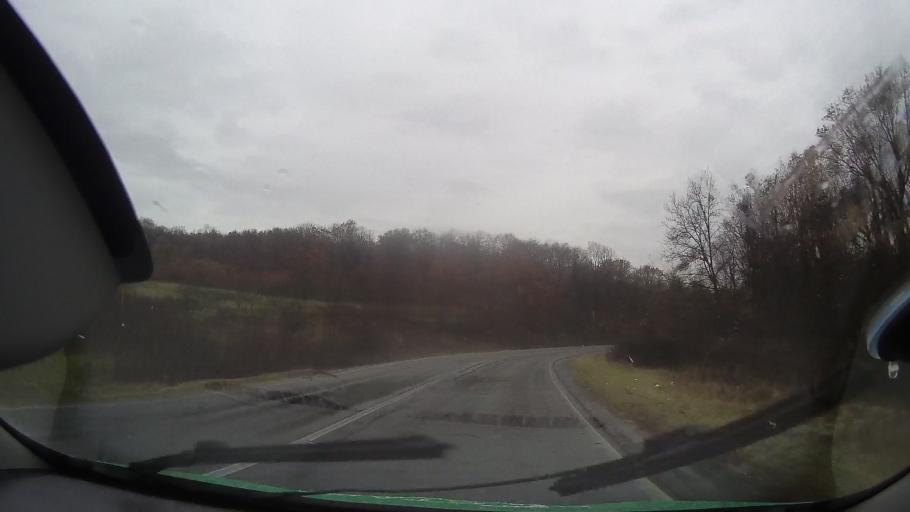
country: RO
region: Bihor
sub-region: Comuna Rabagani
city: Rabagani
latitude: 46.7325
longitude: 22.2309
